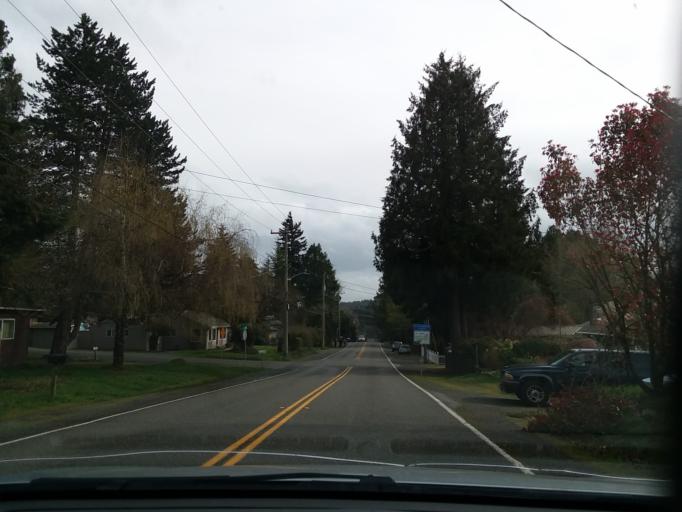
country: US
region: Washington
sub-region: Snohomish County
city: Mountlake Terrace
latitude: 47.7770
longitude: -122.3031
